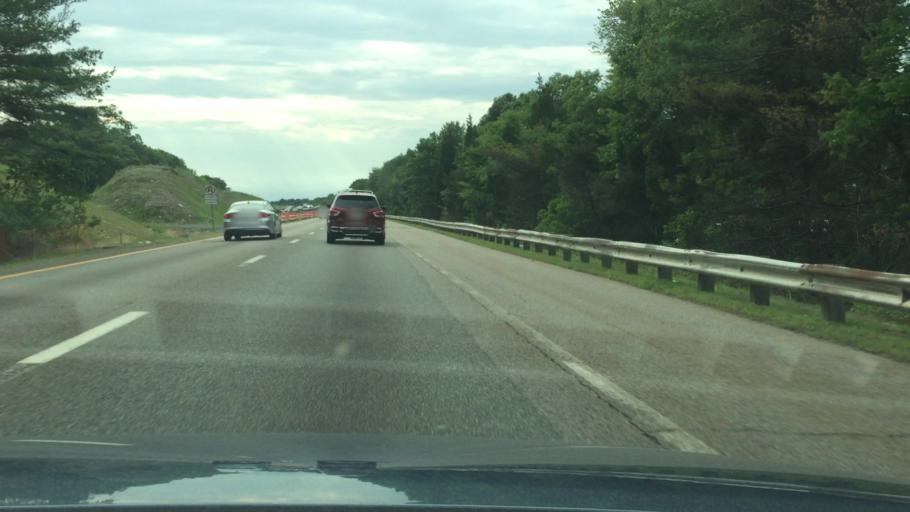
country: US
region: Massachusetts
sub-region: Plymouth County
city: Hanover
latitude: 42.1526
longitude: -70.8484
